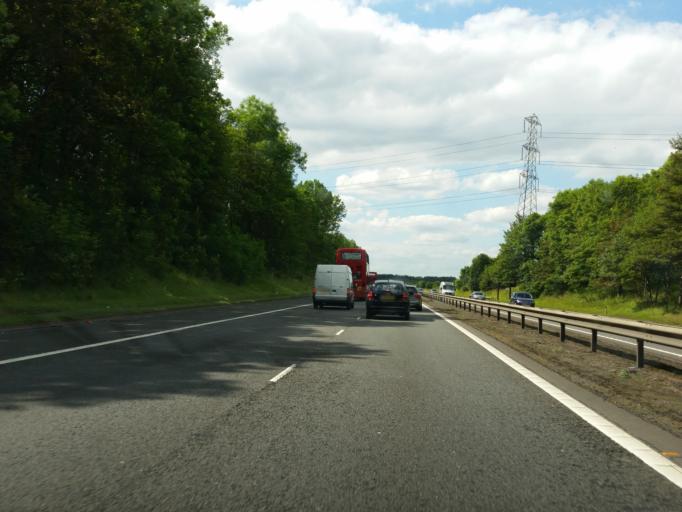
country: GB
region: Scotland
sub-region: North Lanarkshire
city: Motherwell
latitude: 55.7621
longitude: -3.9834
